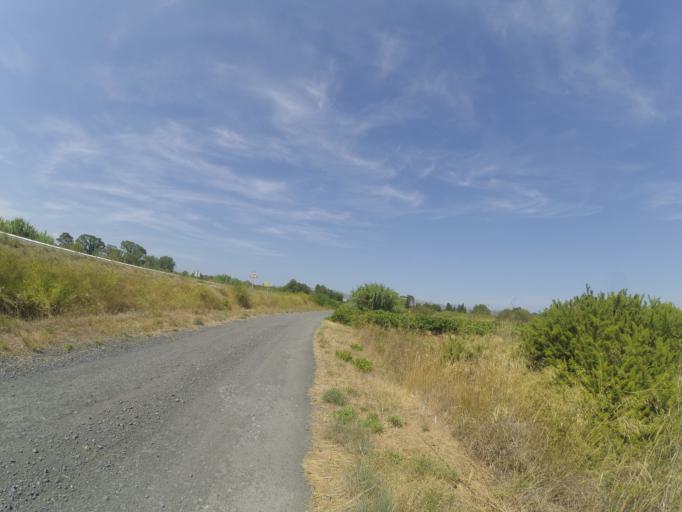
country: FR
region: Languedoc-Roussillon
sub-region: Departement des Pyrenees-Orientales
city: Peyrestortes
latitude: 42.7571
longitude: 2.8574
